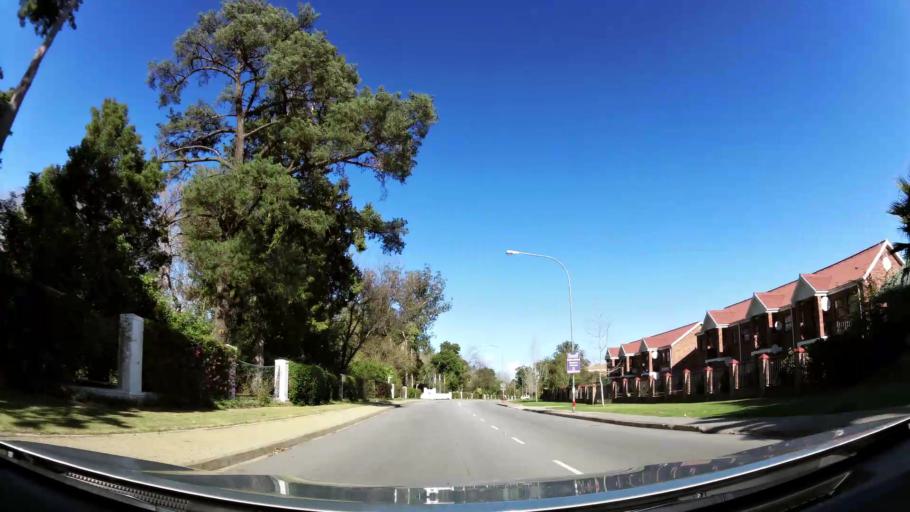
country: ZA
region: Western Cape
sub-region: Eden District Municipality
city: George
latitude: -33.9505
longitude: 22.4069
